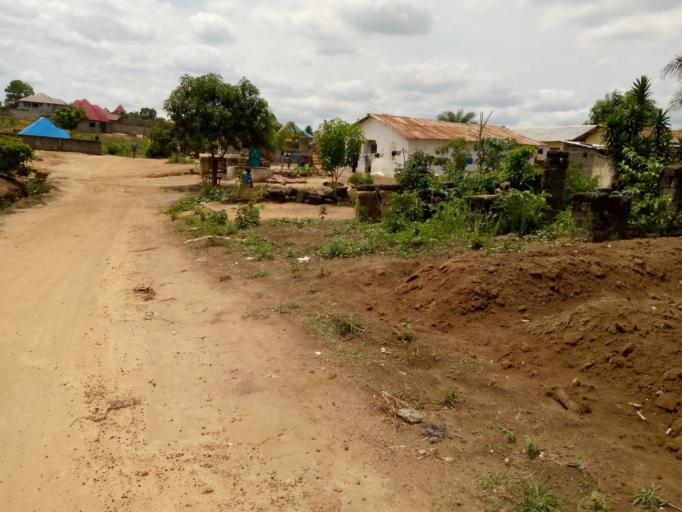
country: SL
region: Western Area
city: Waterloo
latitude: 8.3314
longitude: -13.0339
